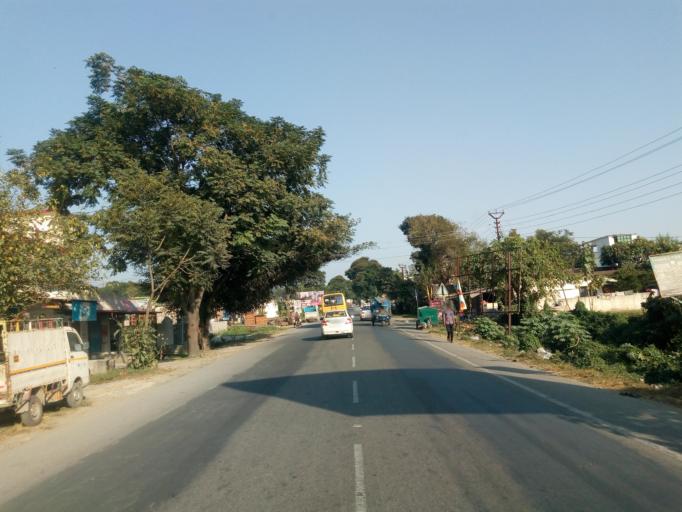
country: IN
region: Uttarakhand
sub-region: Dehradun
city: Dehradun
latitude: 30.3443
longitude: 77.9199
